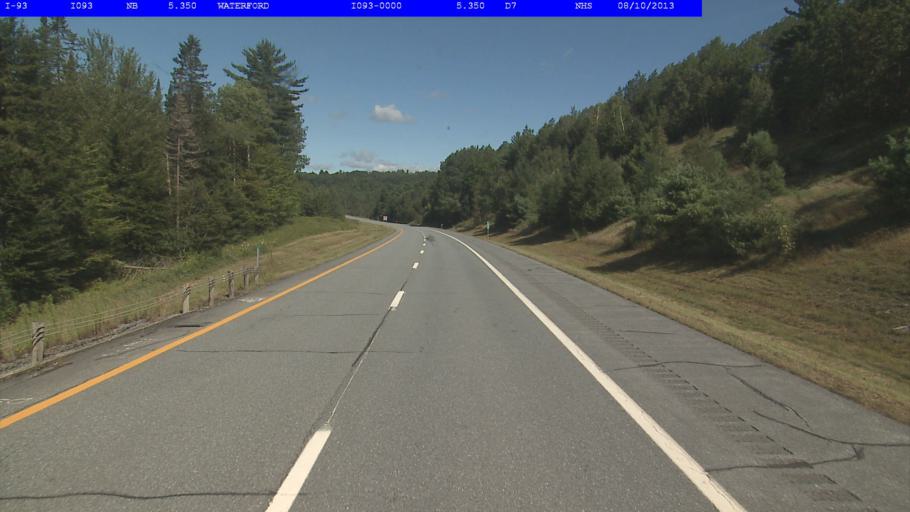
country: US
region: Vermont
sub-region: Caledonia County
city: Saint Johnsbury
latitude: 44.4123
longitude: -71.9213
